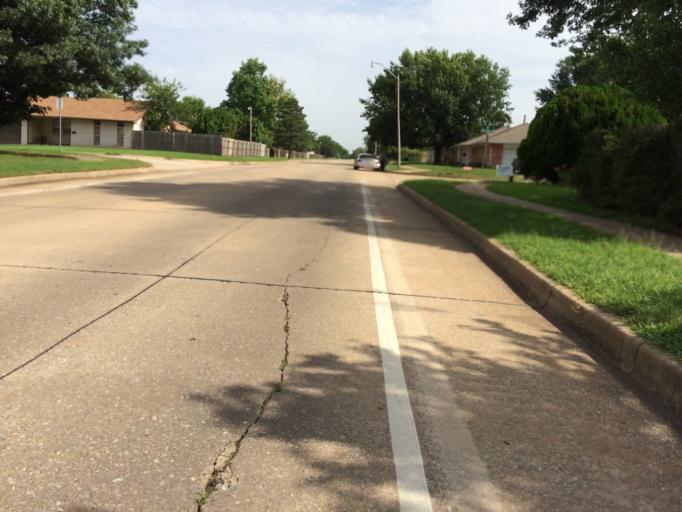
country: US
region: Oklahoma
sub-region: Cleveland County
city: Hall Park
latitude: 35.2152
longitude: -97.4163
